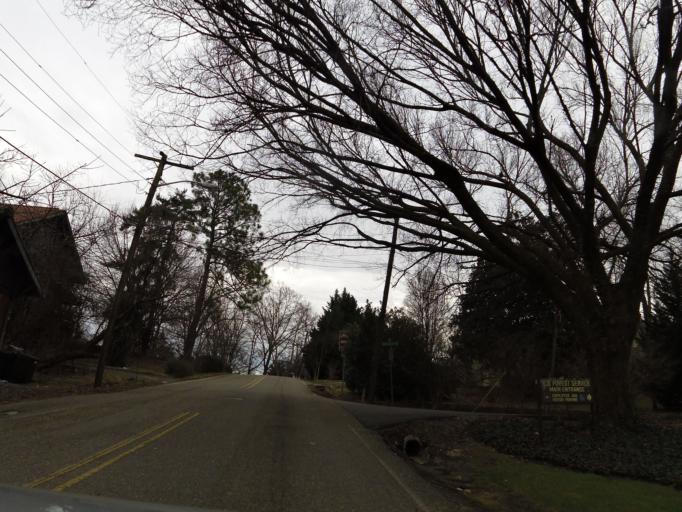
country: US
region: Tennessee
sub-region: Knox County
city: Knoxville
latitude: 35.9395
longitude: -83.9815
